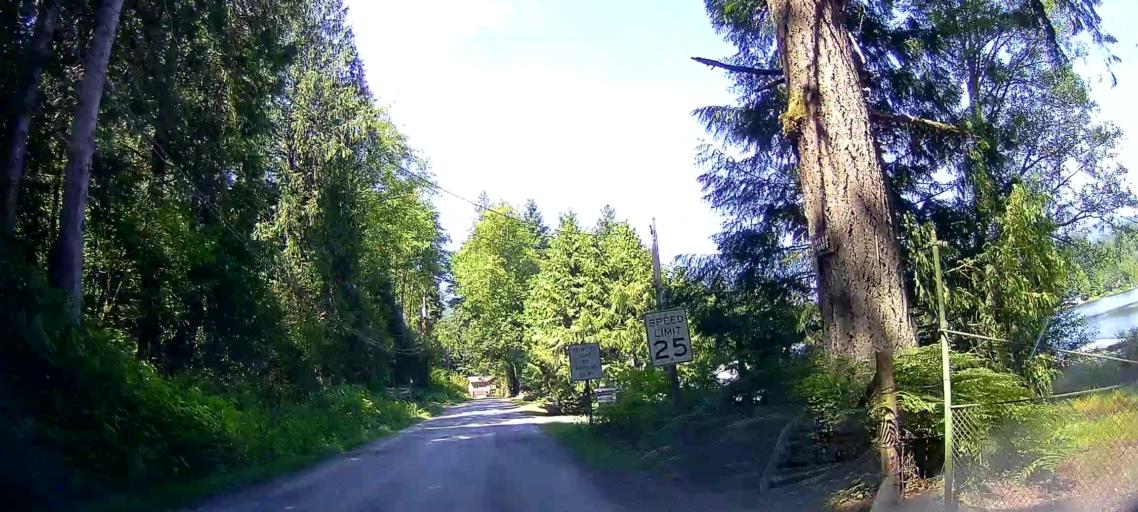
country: US
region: Washington
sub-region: Whatcom County
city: Sudden Valley
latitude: 48.6459
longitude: -122.3301
